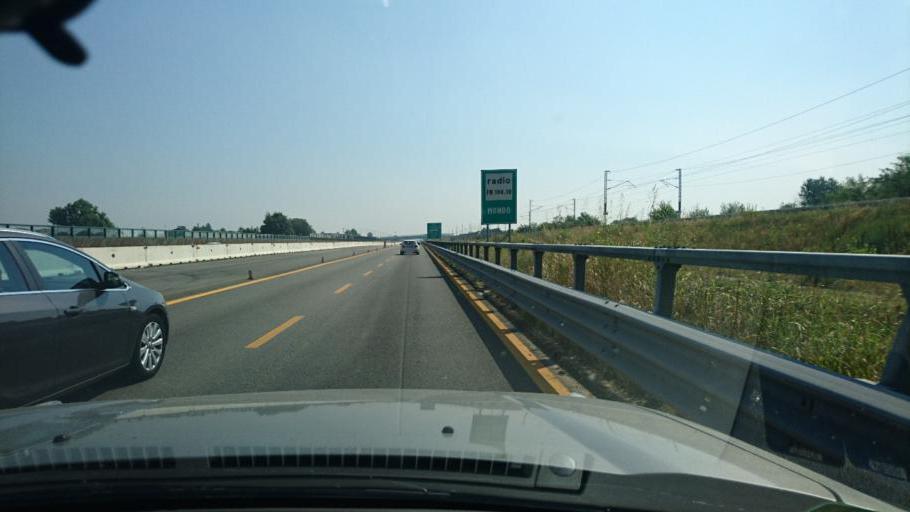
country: IT
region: Piedmont
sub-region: Provincia di Novara
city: Galliate
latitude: 45.4680
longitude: 8.6924
